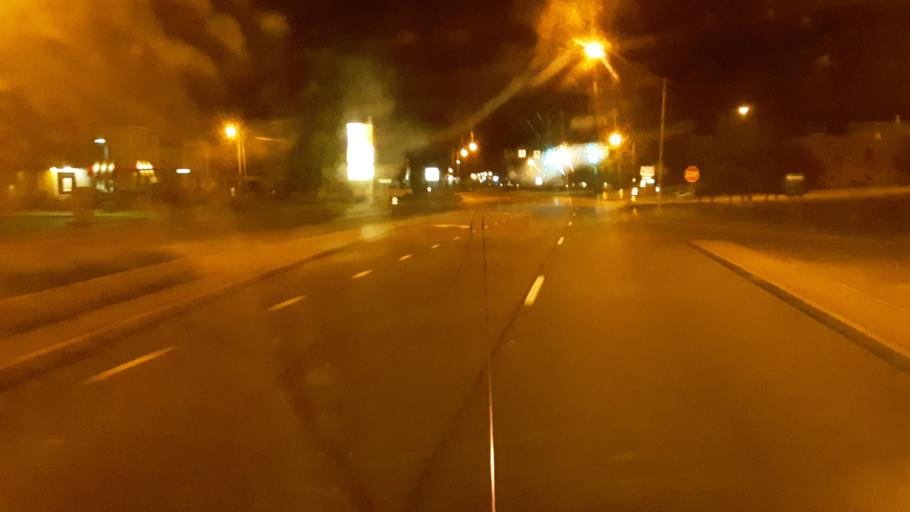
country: US
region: New York
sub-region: Oneida County
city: Rome
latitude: 43.2118
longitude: -75.4613
